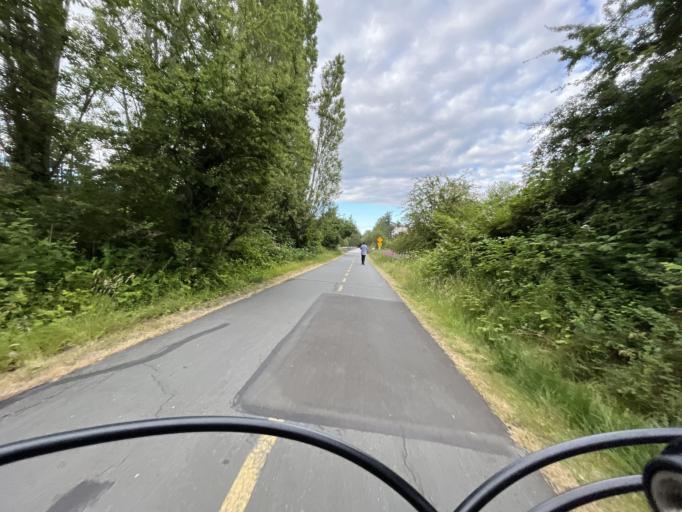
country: CA
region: British Columbia
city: Victoria
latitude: 48.4638
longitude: -123.3673
